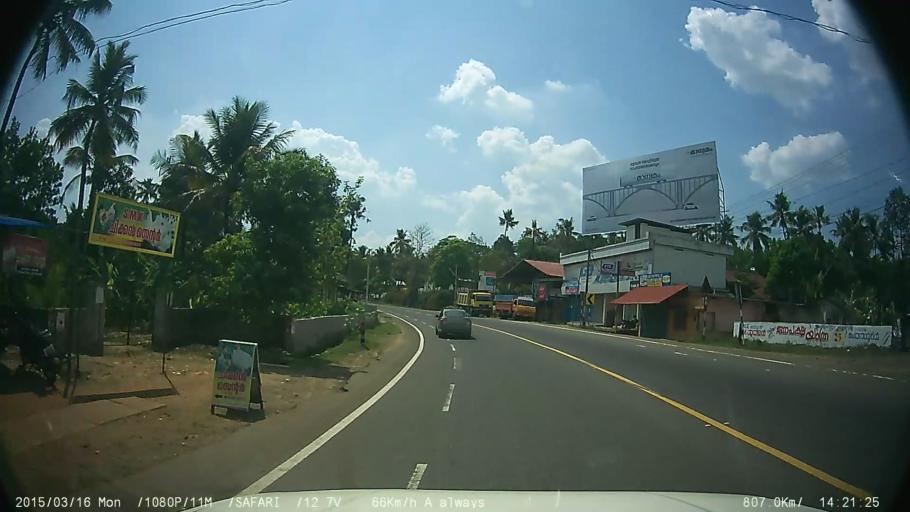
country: IN
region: Kerala
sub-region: Ernakulam
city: Perumbavoor
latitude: 10.0584
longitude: 76.5277
